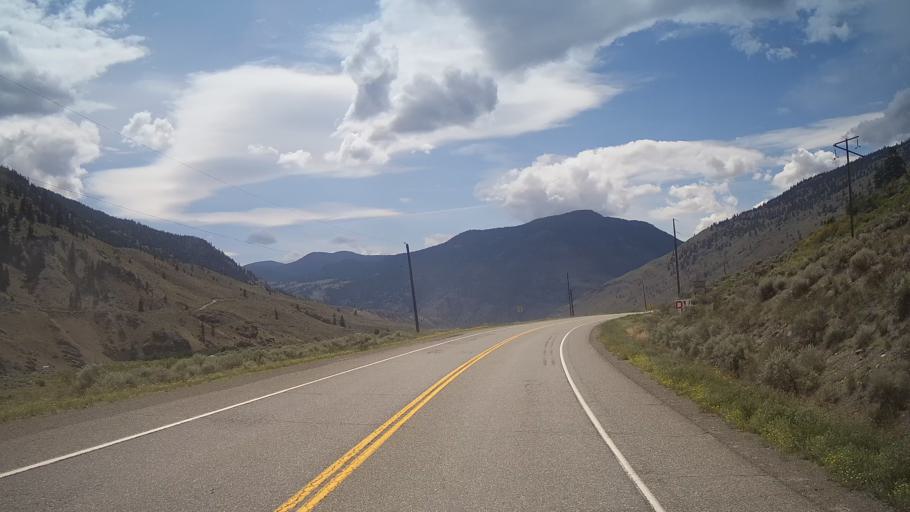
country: CA
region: British Columbia
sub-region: Thompson-Nicola Regional District
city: Ashcroft
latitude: 50.4606
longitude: -121.3020
